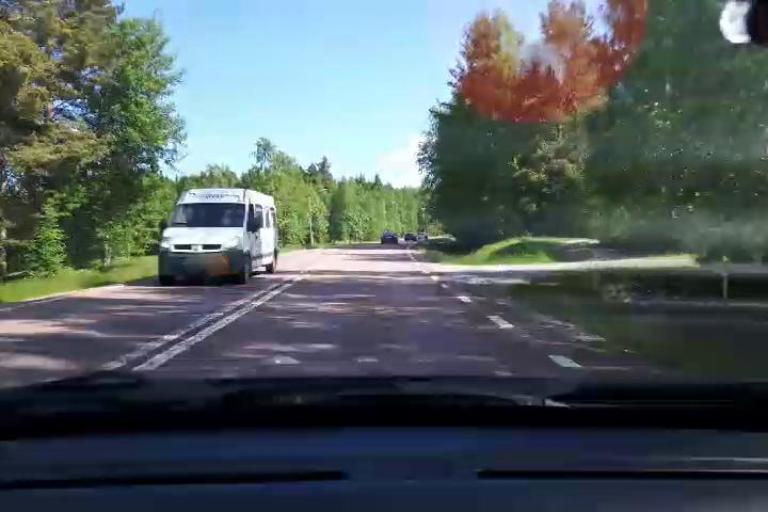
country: SE
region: Gaevleborg
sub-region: Hudiksvalls Kommun
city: Delsbo
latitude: 61.8009
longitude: 16.4907
